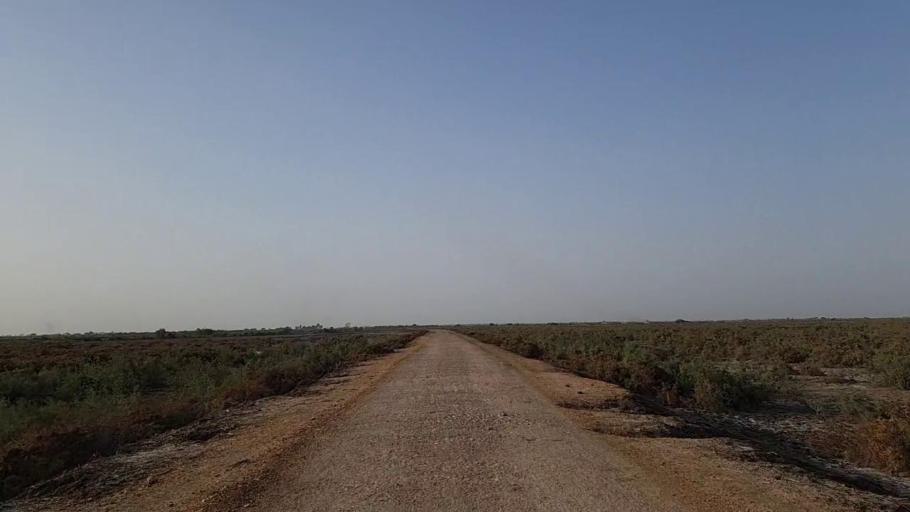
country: PK
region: Sindh
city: Jati
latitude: 24.3592
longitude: 68.1469
